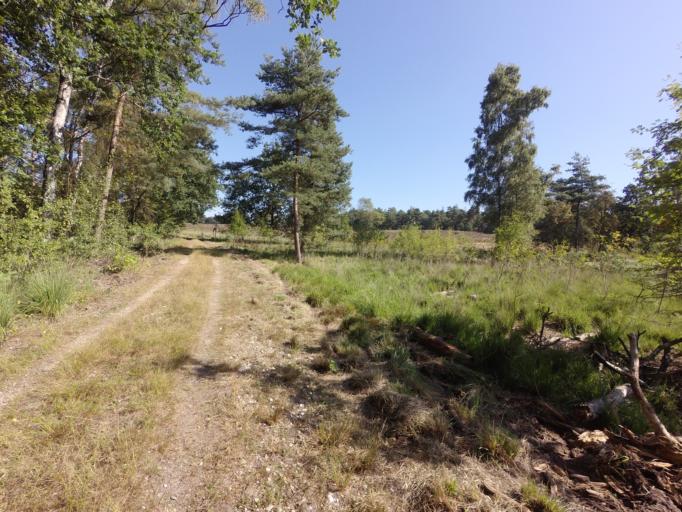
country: DE
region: North Rhine-Westphalia
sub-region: Regierungsbezirk Koln
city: Wassenberg
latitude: 51.1552
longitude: 6.1335
